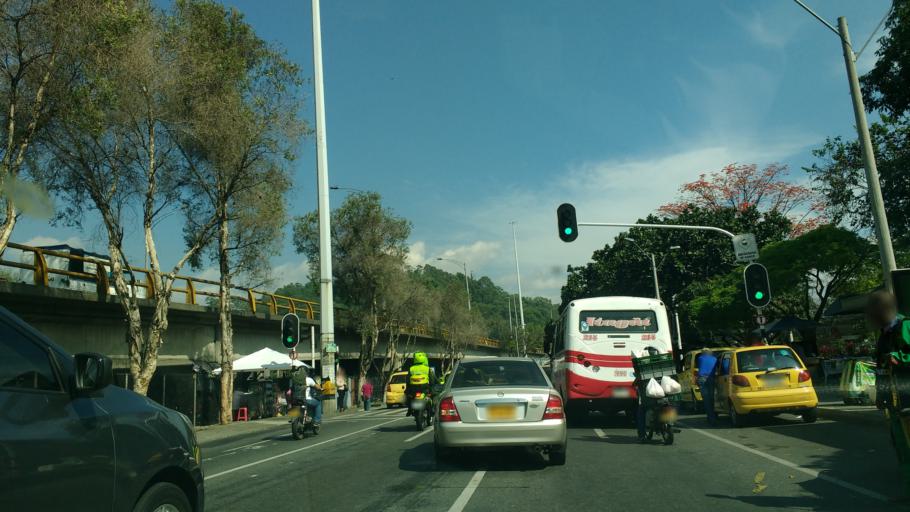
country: CO
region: Antioquia
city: Medellin
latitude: 6.2307
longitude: -75.5771
